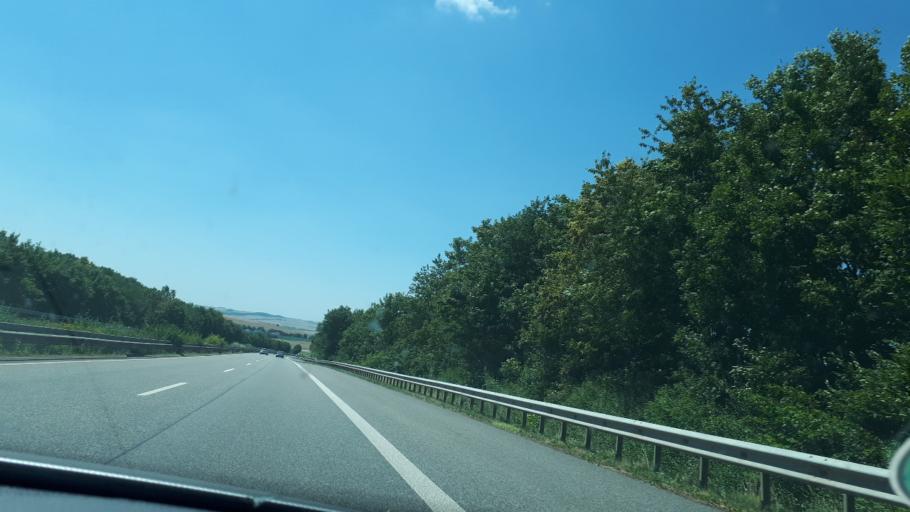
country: DE
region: Rheinland-Pfalz
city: Kerben
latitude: 50.3226
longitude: 7.3667
